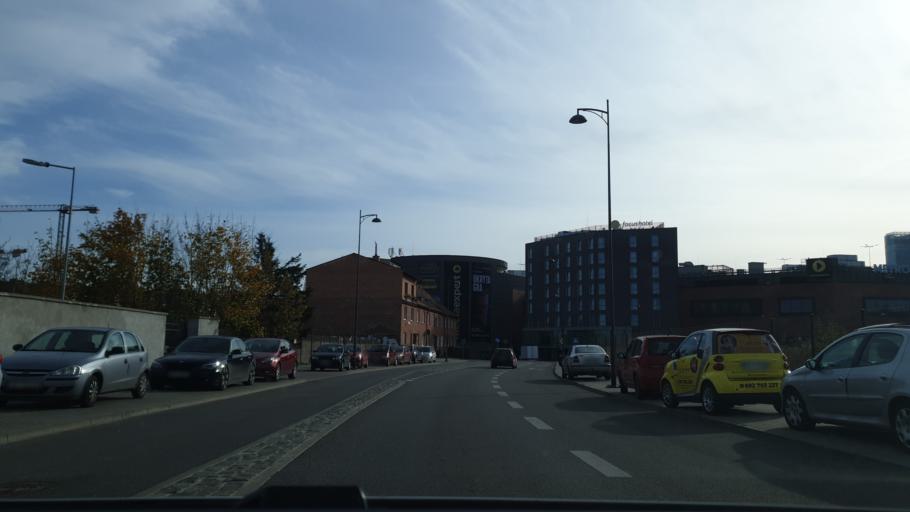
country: PL
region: Pomeranian Voivodeship
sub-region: Gdansk
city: Gdansk
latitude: 54.3847
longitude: 18.6034
